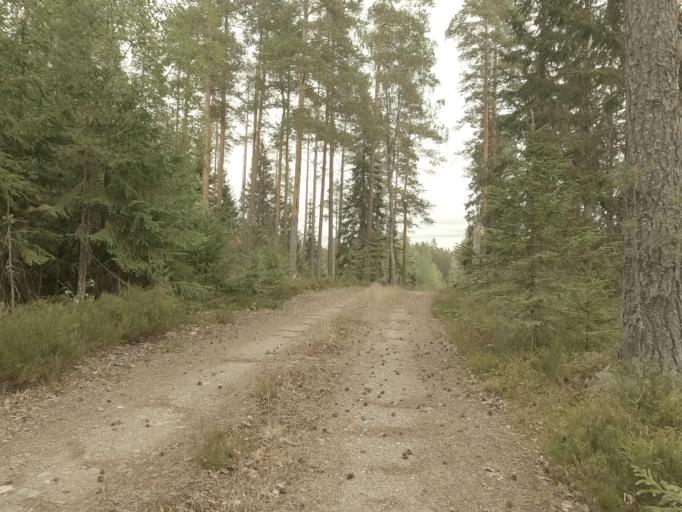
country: RU
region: Leningrad
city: Kamennogorsk
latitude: 61.0205
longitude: 29.1777
